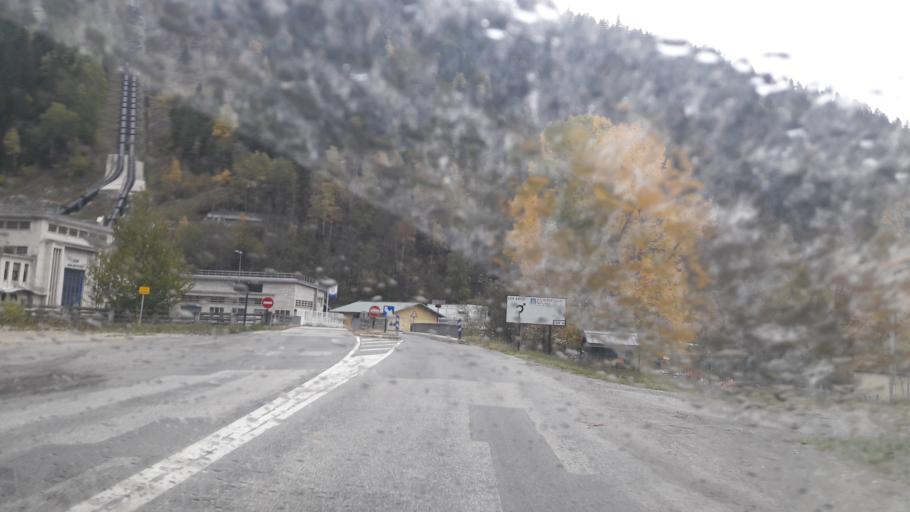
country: FR
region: Rhone-Alpes
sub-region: Departement de la Savoie
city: Seez
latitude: 45.6191
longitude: 6.7888
